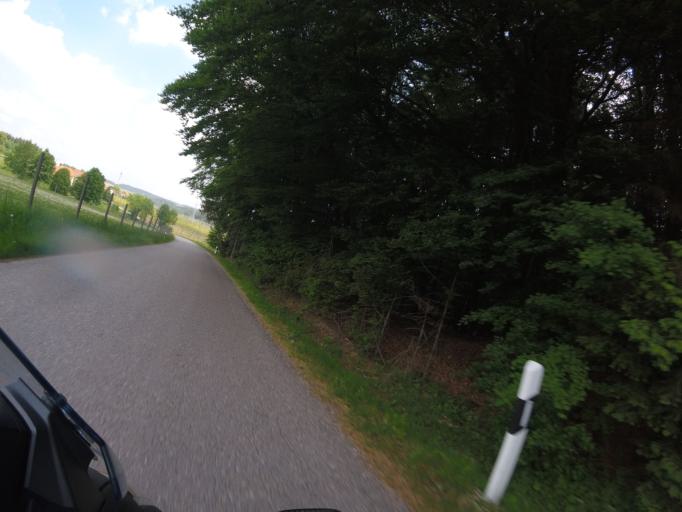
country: DE
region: Bavaria
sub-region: Upper Bavaria
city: Rudelzhausen
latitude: 48.6123
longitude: 11.7117
